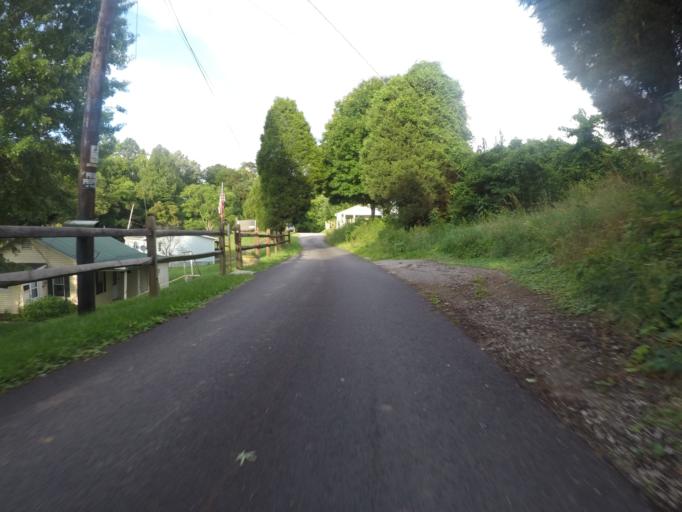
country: US
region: West Virginia
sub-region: Cabell County
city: Pea Ridge
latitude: 38.4066
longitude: -82.3628
